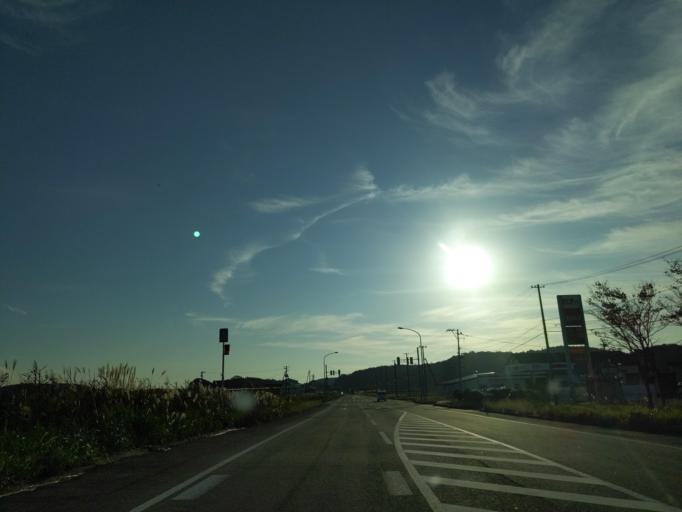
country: JP
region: Niigata
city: Nagaoka
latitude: 37.5756
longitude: 138.7490
